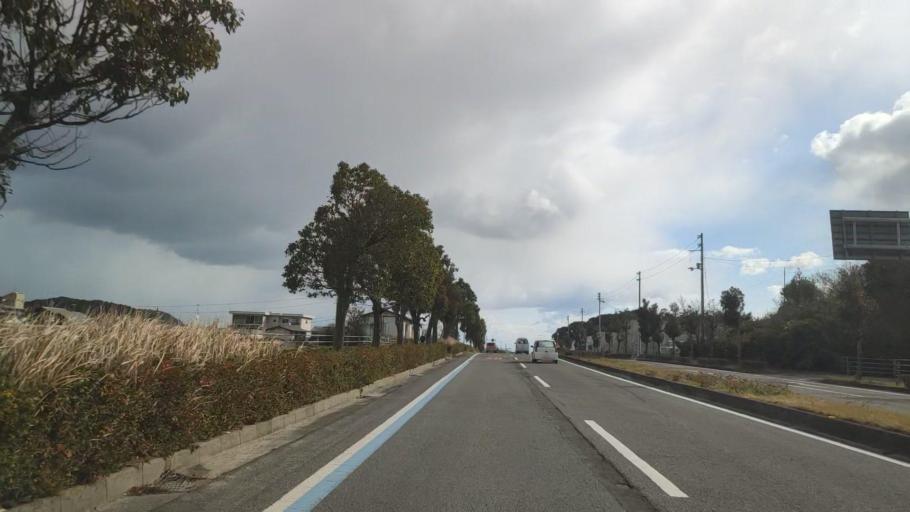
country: JP
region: Ehime
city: Hojo
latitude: 34.0624
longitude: 132.9581
